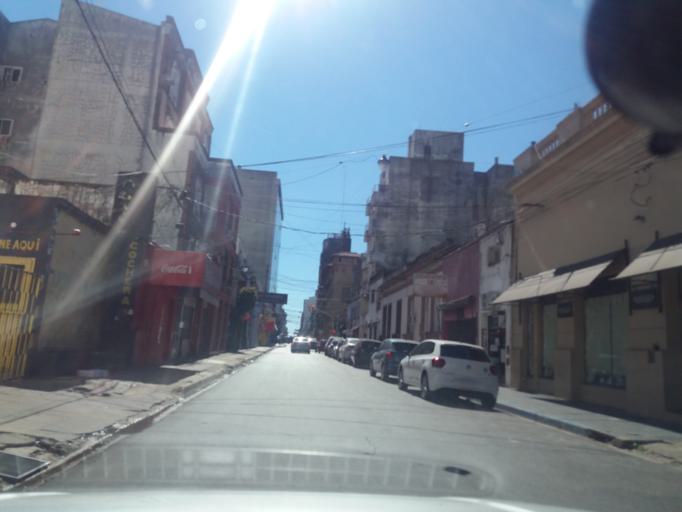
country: AR
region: Corrientes
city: Corrientes
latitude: -27.4694
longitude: -58.8358
